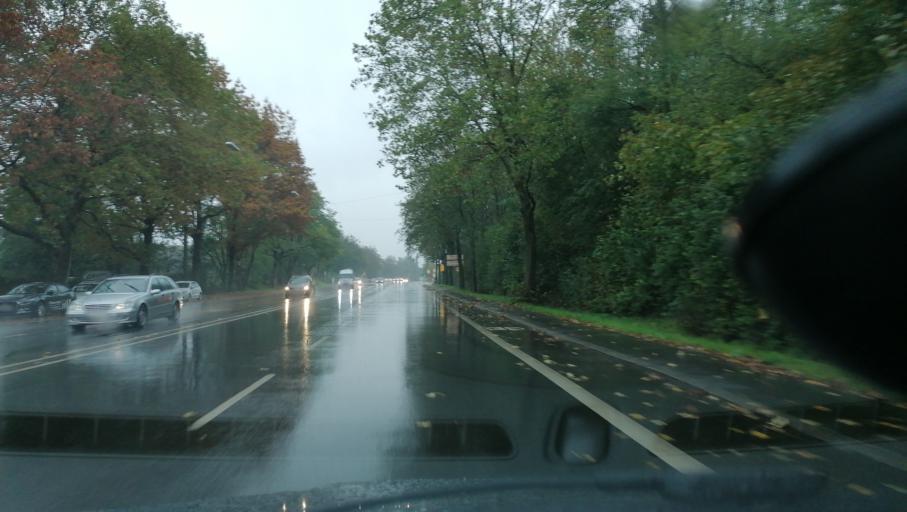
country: DE
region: North Rhine-Westphalia
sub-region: Regierungsbezirk Munster
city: Recklinghausen
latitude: 51.5956
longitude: 7.1824
